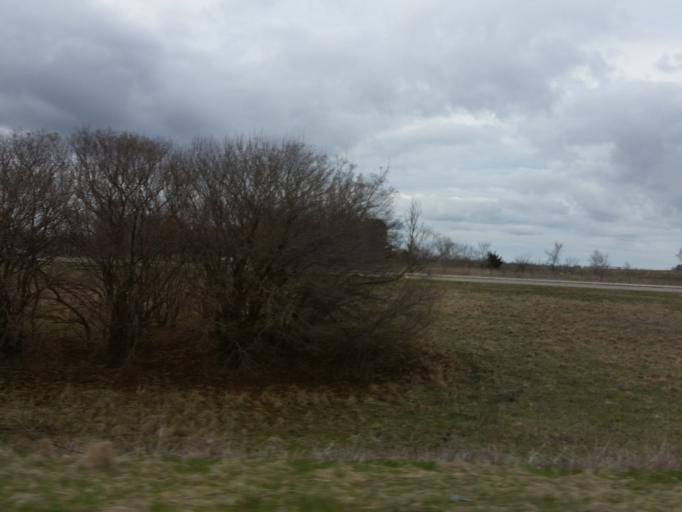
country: US
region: Iowa
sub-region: Black Hawk County
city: Elk Run Heights
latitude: 42.4486
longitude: -92.2167
